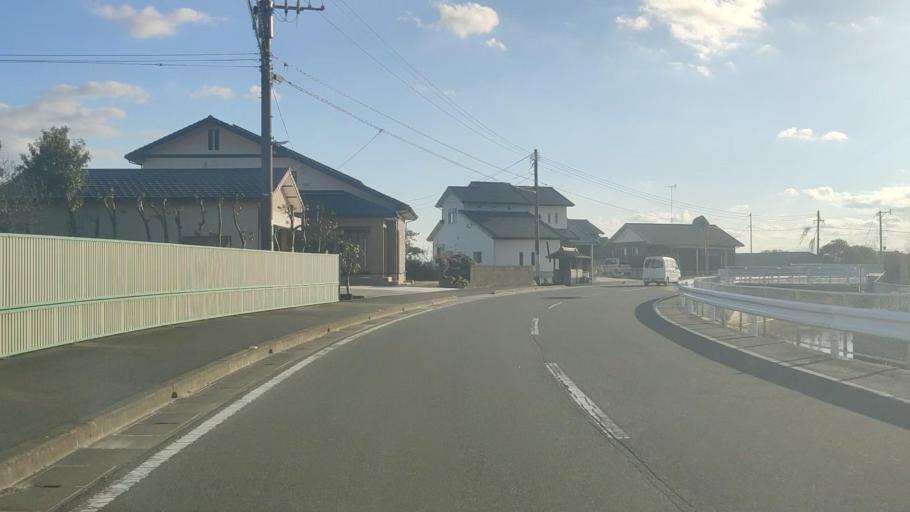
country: JP
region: Saga Prefecture
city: Saga-shi
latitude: 33.3063
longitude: 130.2585
